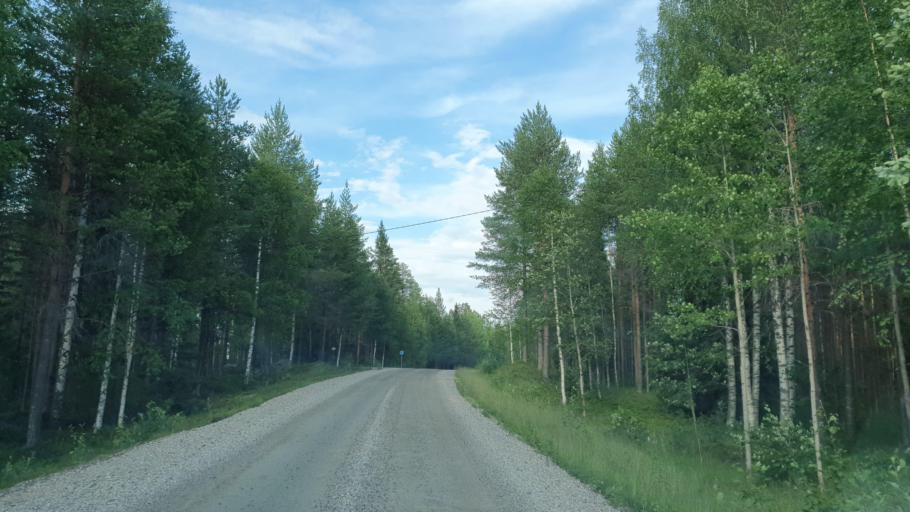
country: FI
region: Kainuu
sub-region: Kehys-Kainuu
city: Kuhmo
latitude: 64.2894
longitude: 29.4739
